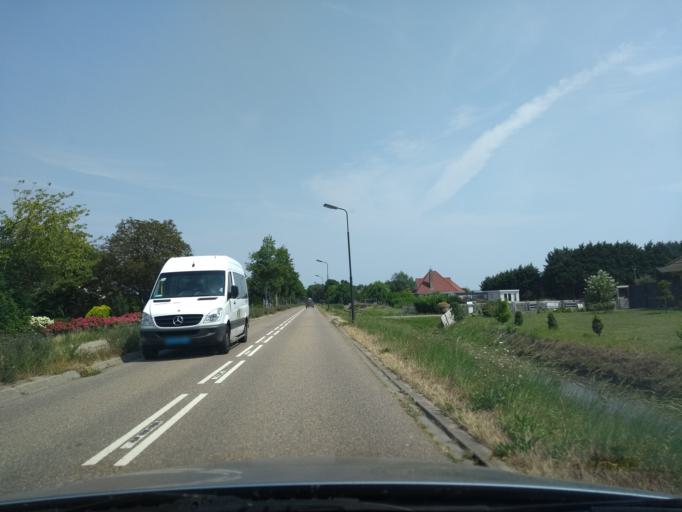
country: NL
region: North Holland
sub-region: Gemeente Heerhugowaard
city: Heerhugowaard
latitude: 52.6464
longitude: 4.8370
